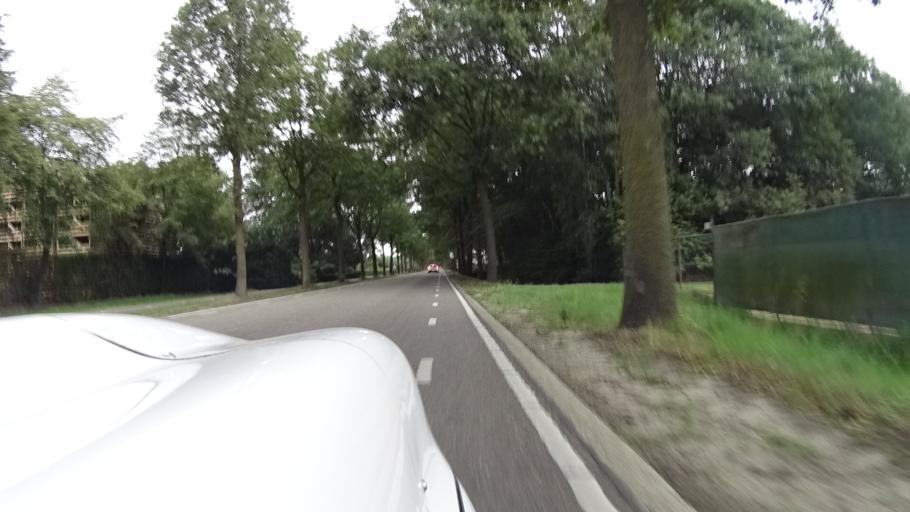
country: NL
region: North Brabant
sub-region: Gemeente Veghel
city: Erp
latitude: 51.6218
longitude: 5.6087
